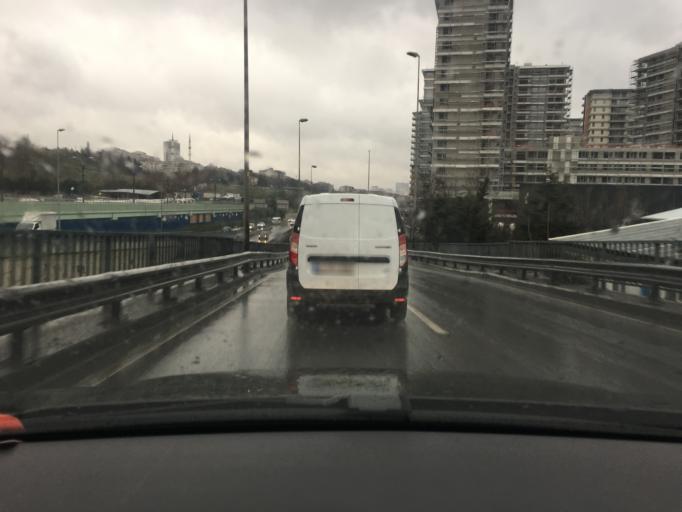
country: TR
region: Istanbul
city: merter keresteciler
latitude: 41.0213
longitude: 28.9005
